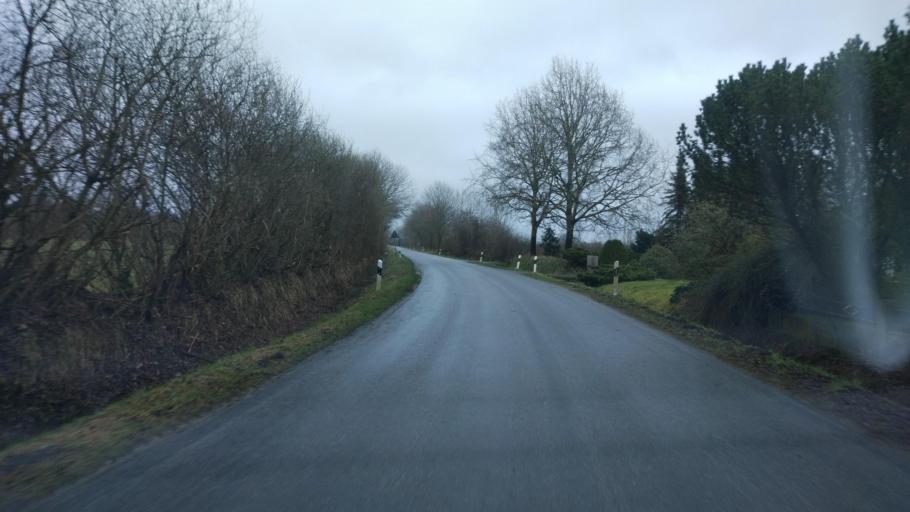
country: DE
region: Schleswig-Holstein
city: Ellingstedt
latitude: 54.4824
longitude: 9.3858
